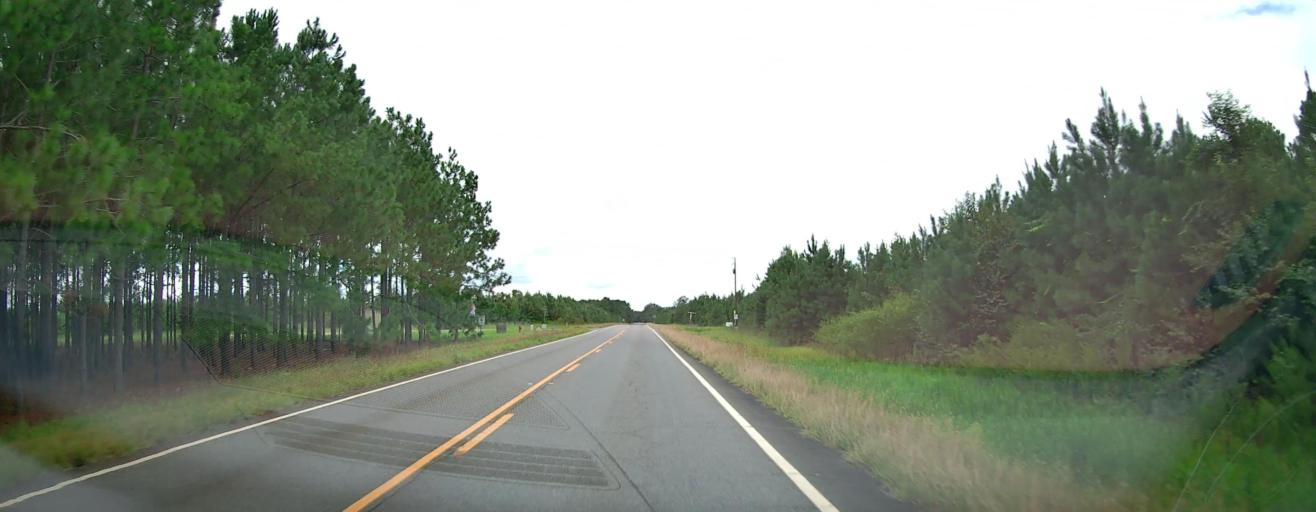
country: US
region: Georgia
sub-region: Marion County
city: Buena Vista
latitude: 32.2679
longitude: -84.4308
